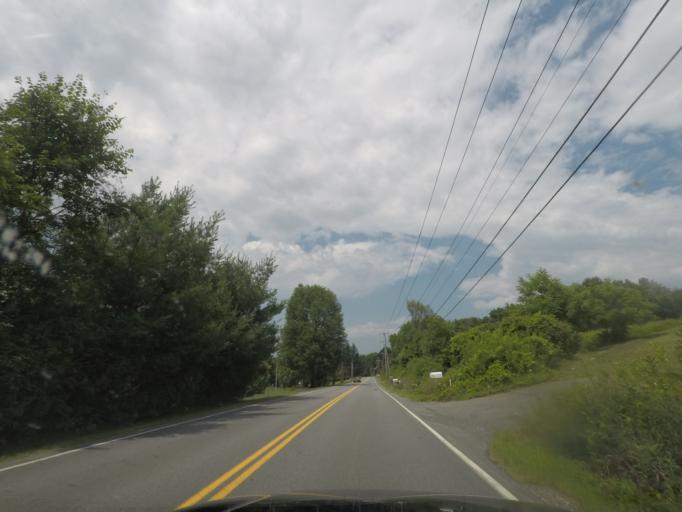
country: US
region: New York
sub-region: Rensselaer County
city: Hampton Manor
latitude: 42.6427
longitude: -73.6820
